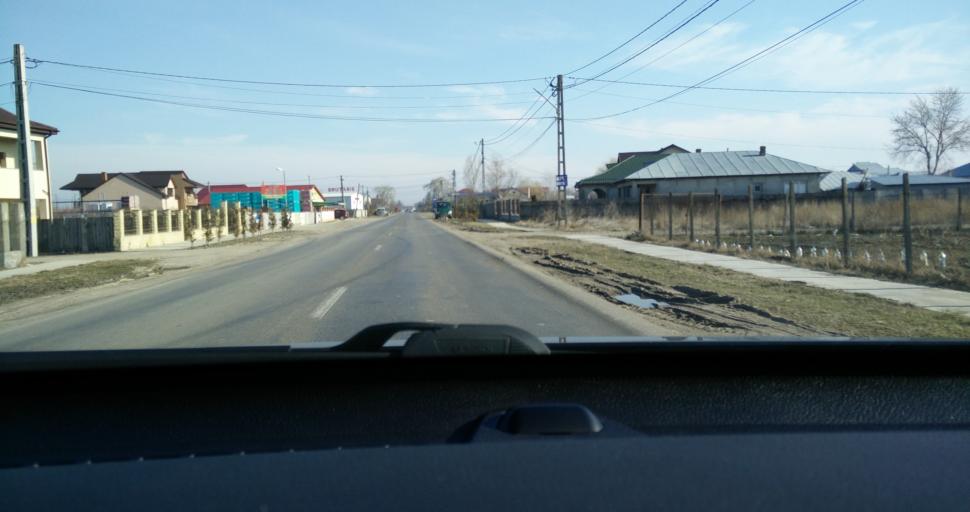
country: RO
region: Vrancea
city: Vulturu de Sus
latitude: 45.6245
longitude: 27.3999
